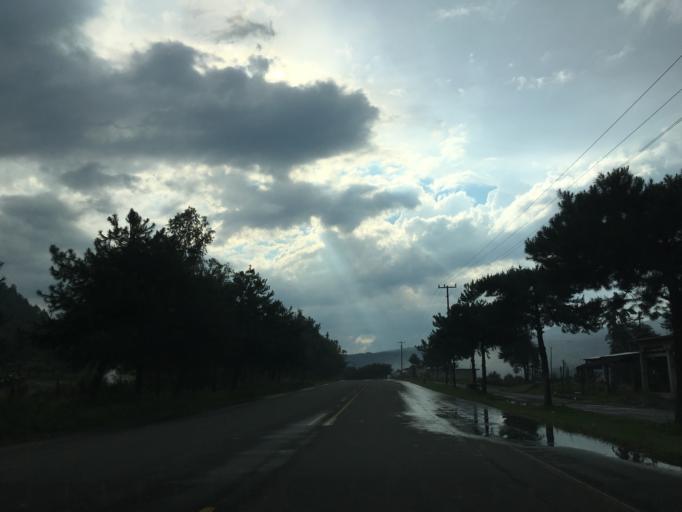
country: MX
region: Michoacan
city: Capacuaro
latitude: 19.5311
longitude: -102.0935
